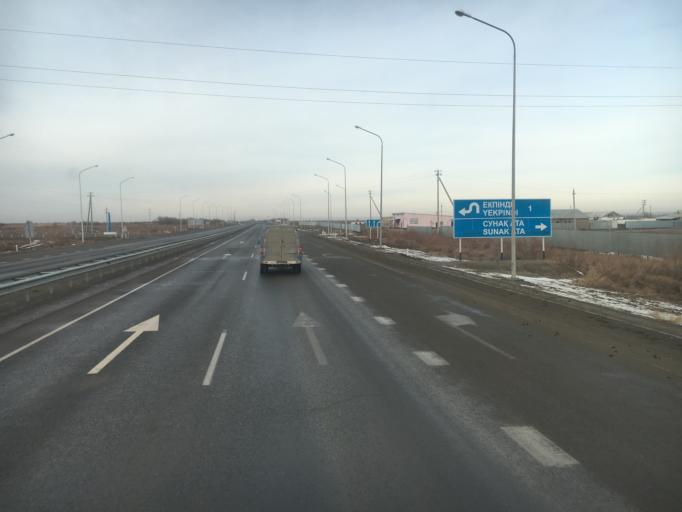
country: KZ
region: Qyzylorda
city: Shieli
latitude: 44.1393
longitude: 66.9659
